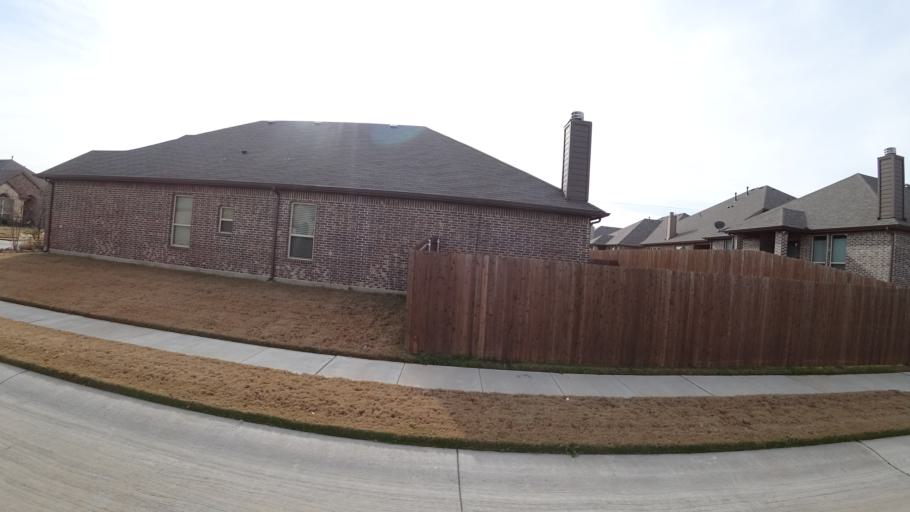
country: US
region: Texas
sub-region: Denton County
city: Highland Village
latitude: 33.0754
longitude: -97.0281
